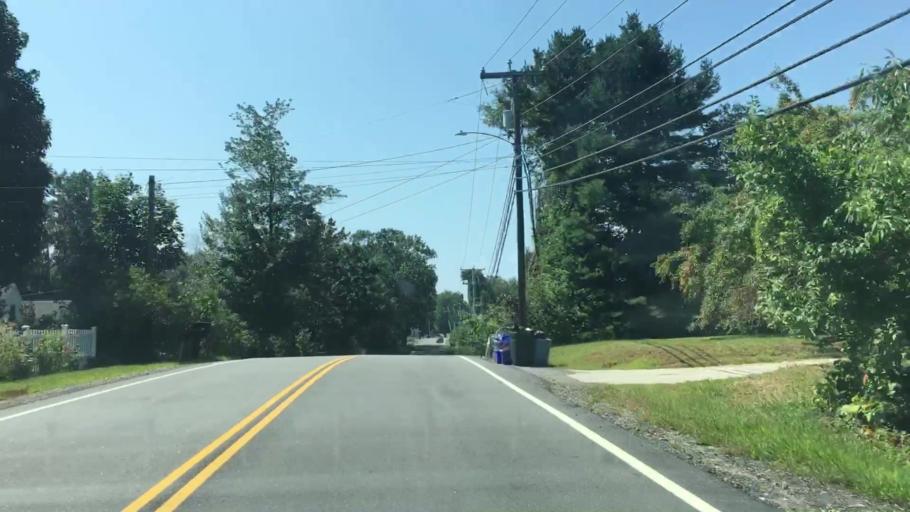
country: US
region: New Hampshire
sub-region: Rockingham County
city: Hampstead
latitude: 42.8793
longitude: -71.1674
